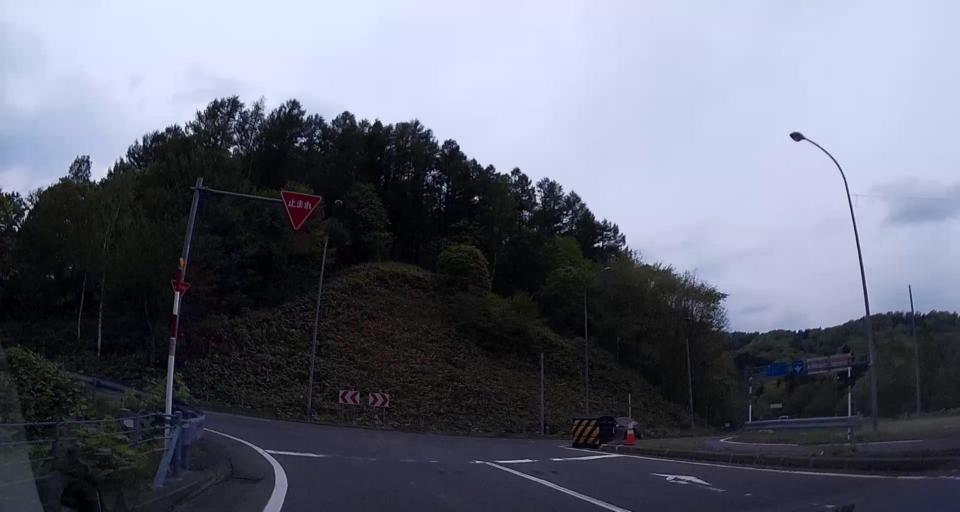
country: JP
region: Hokkaido
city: Shiraoi
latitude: 42.6953
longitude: 141.1064
